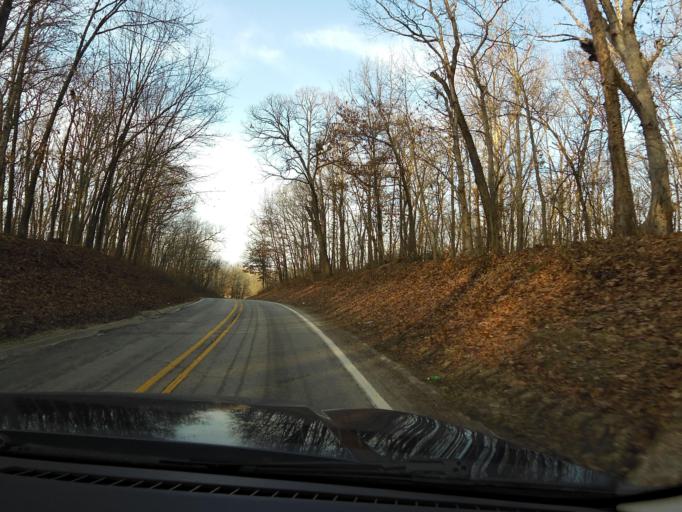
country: US
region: Illinois
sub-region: Fayette County
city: Vandalia
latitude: 38.9218
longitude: -89.2333
